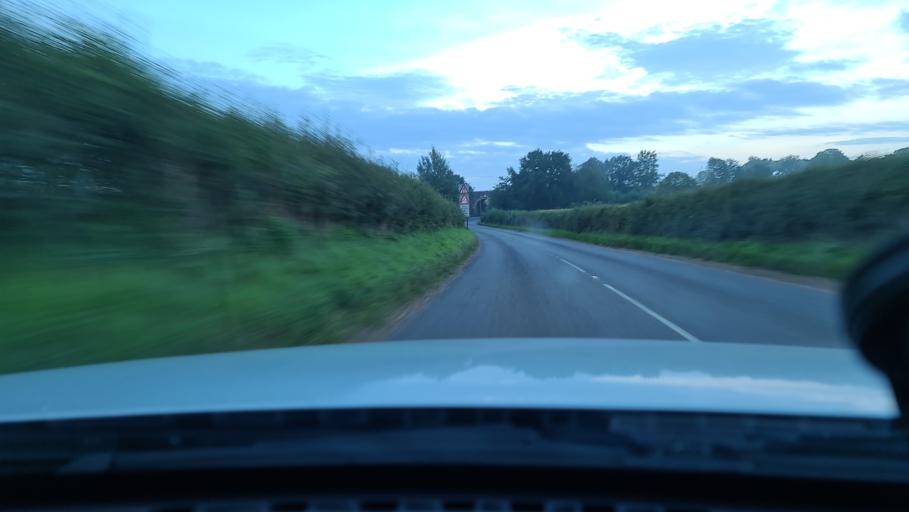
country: GB
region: England
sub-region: Warwickshire
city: Wolston
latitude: 52.3824
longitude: -1.3730
